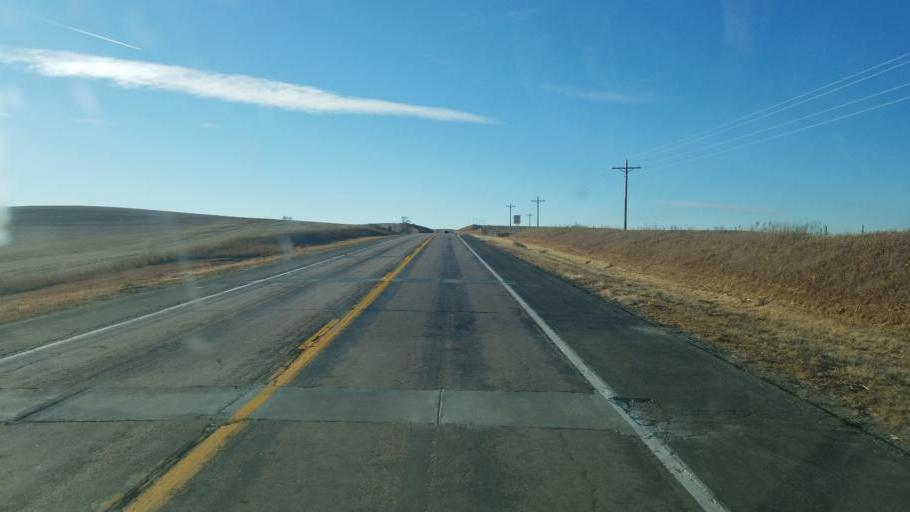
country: US
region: Nebraska
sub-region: Dixon County
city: Ponca
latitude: 42.4738
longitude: -96.6498
